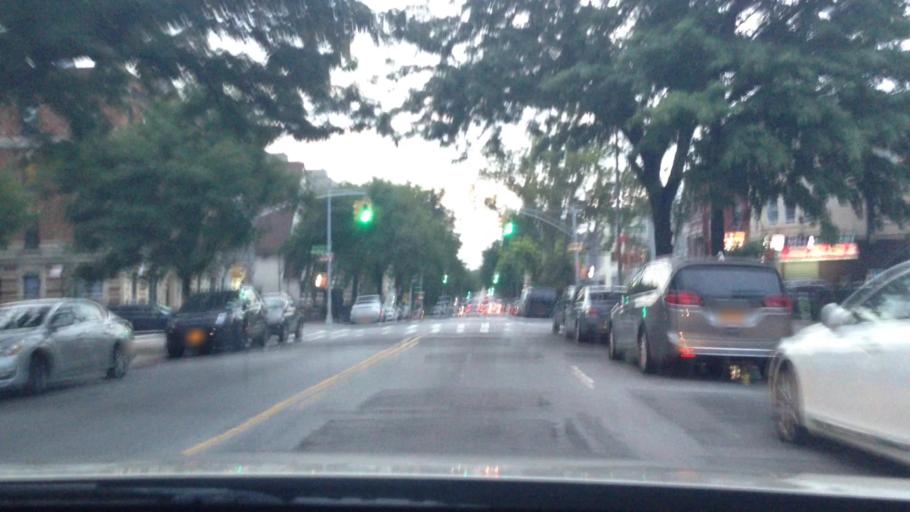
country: US
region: New York
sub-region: Kings County
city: East New York
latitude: 40.6882
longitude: -73.9158
